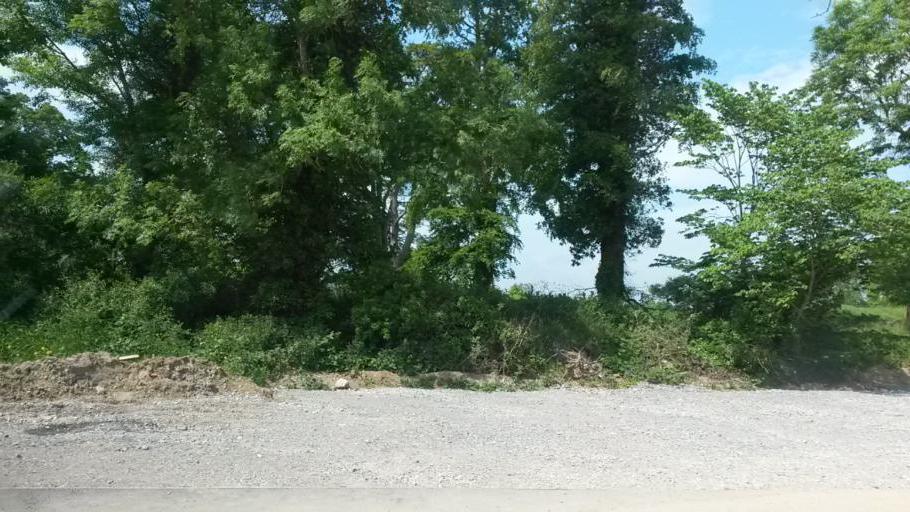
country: IE
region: Leinster
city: Donabate
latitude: 53.4914
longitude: -6.1622
